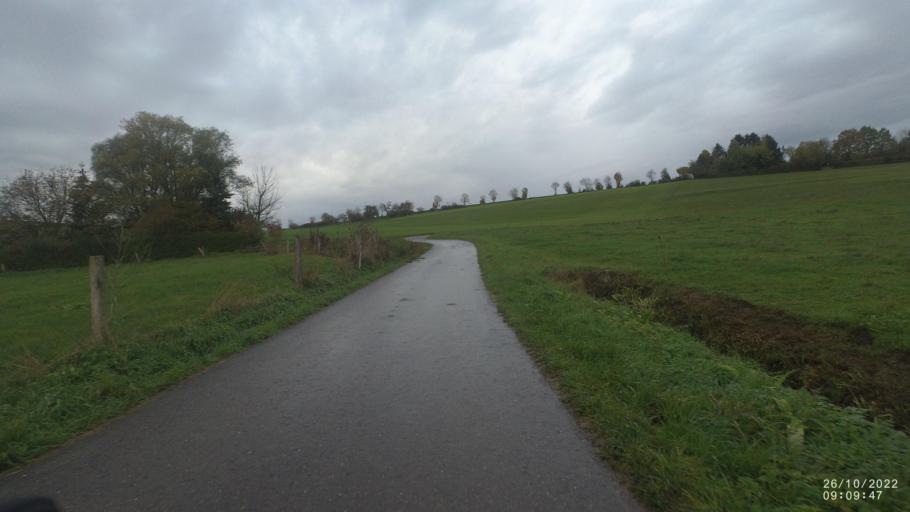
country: DE
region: Baden-Wuerttemberg
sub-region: Regierungsbezirk Stuttgart
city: Heiningen
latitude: 48.6763
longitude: 9.6640
